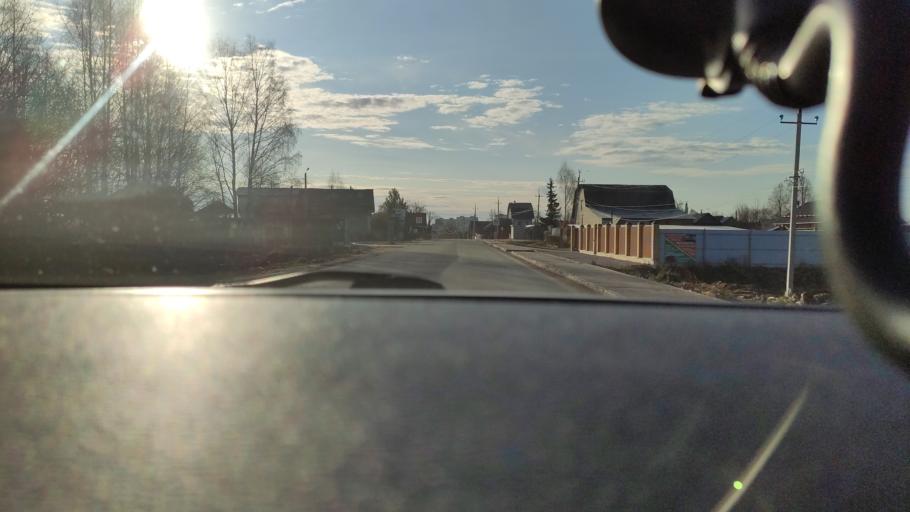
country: RU
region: Perm
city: Kondratovo
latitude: 58.0544
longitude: 56.0282
